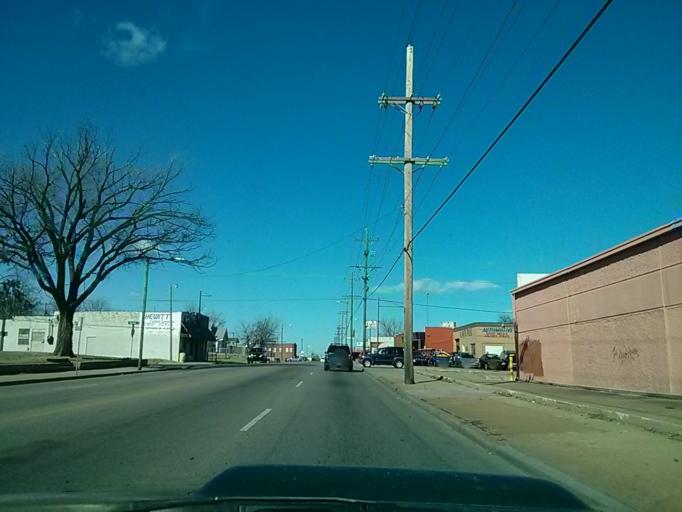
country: US
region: Oklahoma
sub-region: Tulsa County
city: Tulsa
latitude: 36.1621
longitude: -95.9581
